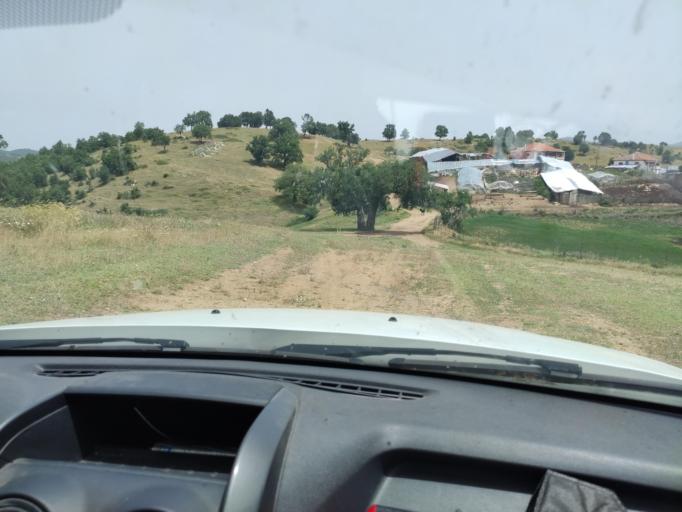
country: MK
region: Radovis
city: Radovish
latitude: 41.6789
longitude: 22.4015
